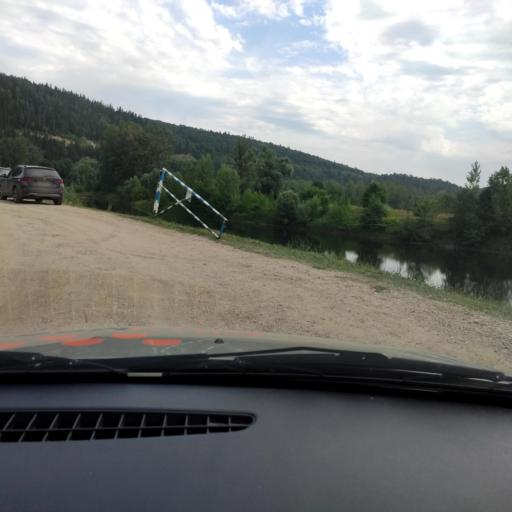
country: RU
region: Bashkortostan
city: Krasnyy Klyuch
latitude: 55.3786
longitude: 56.6740
